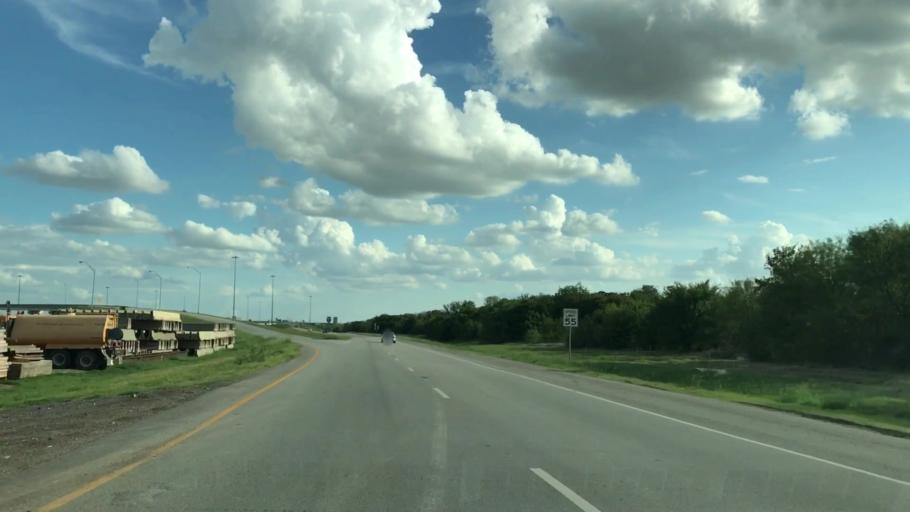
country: US
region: Texas
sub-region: Dallas County
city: Coppell
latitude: 32.9544
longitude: -97.0419
